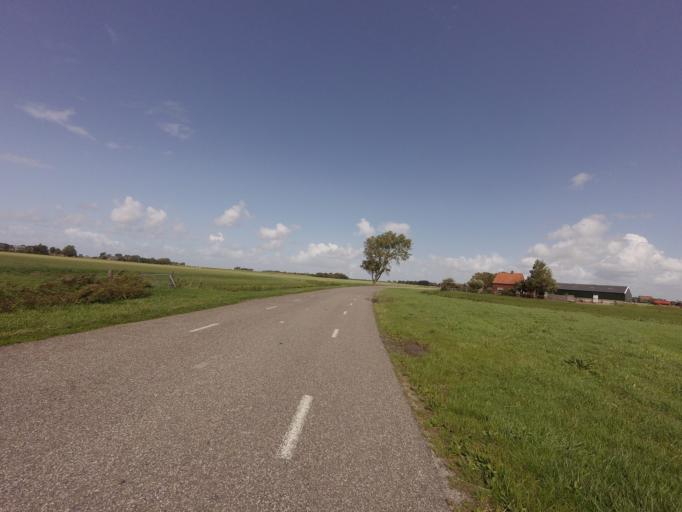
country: NL
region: Friesland
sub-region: Sudwest Fryslan
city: Makkum
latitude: 53.1066
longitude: 5.4323
